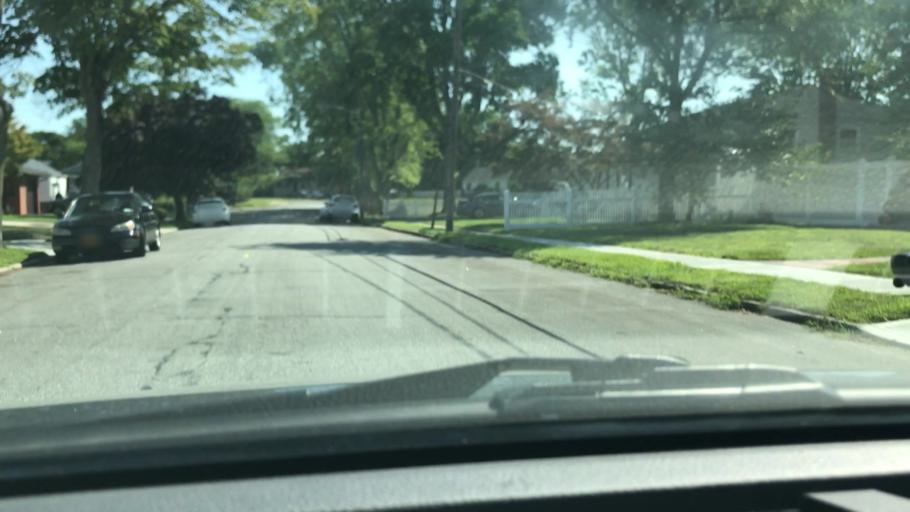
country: US
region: New York
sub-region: Suffolk County
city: North Lindenhurst
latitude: 40.7096
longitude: -73.3855
